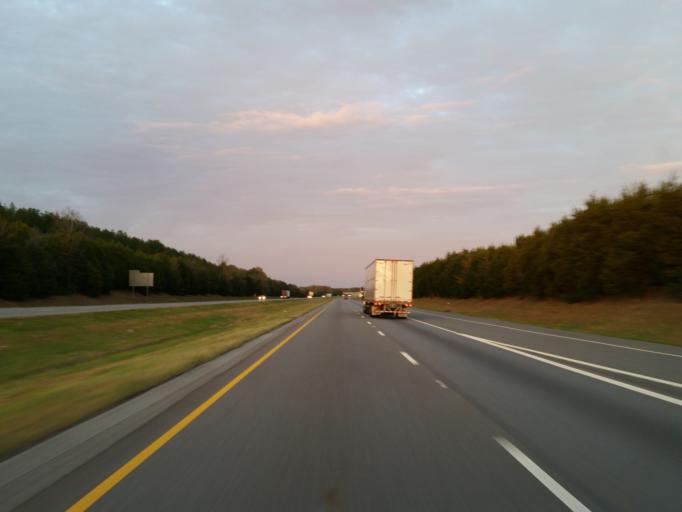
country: US
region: Alabama
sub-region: Sumter County
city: Livingston
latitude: 32.7039
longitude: -88.1393
